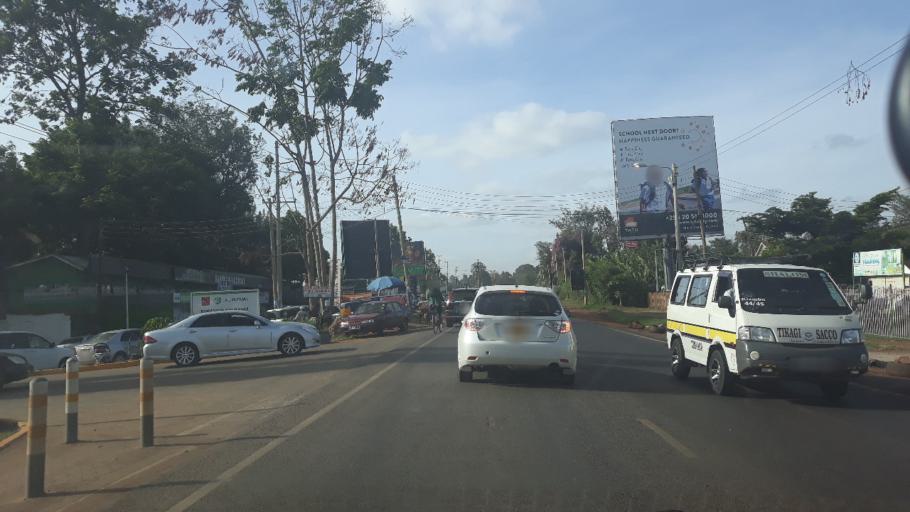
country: KE
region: Nairobi Area
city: Pumwani
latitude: -1.2291
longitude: 36.8406
